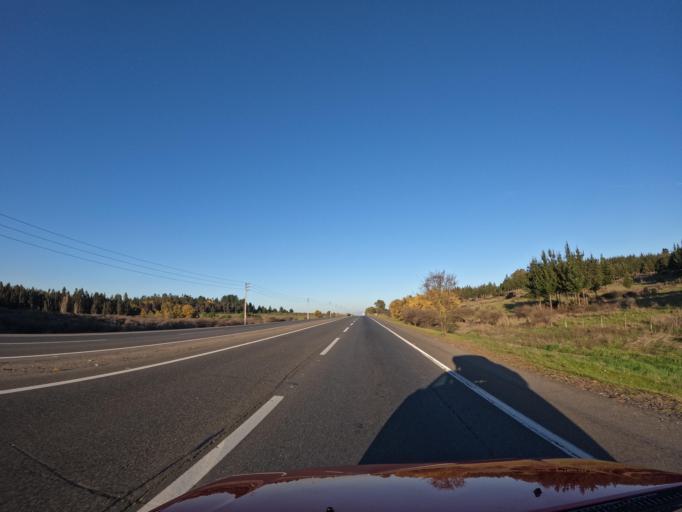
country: CL
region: Biobio
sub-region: Provincia de Nuble
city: Bulnes
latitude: -36.6589
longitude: -72.2939
